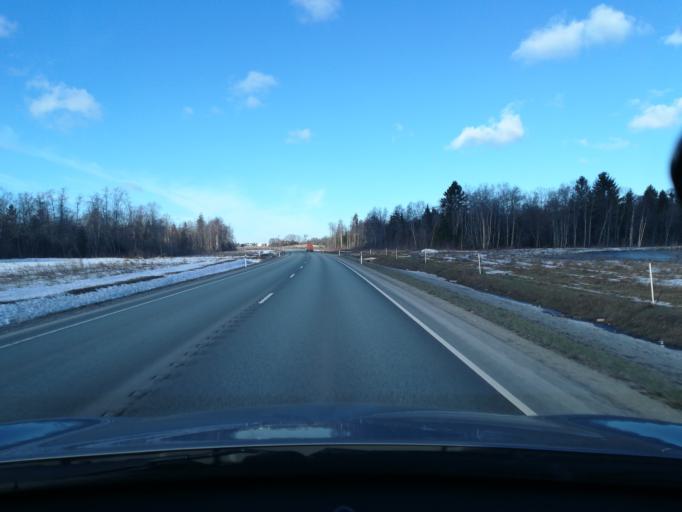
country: EE
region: Harju
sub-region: Saku vald
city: Saku
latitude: 59.3245
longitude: 24.6382
